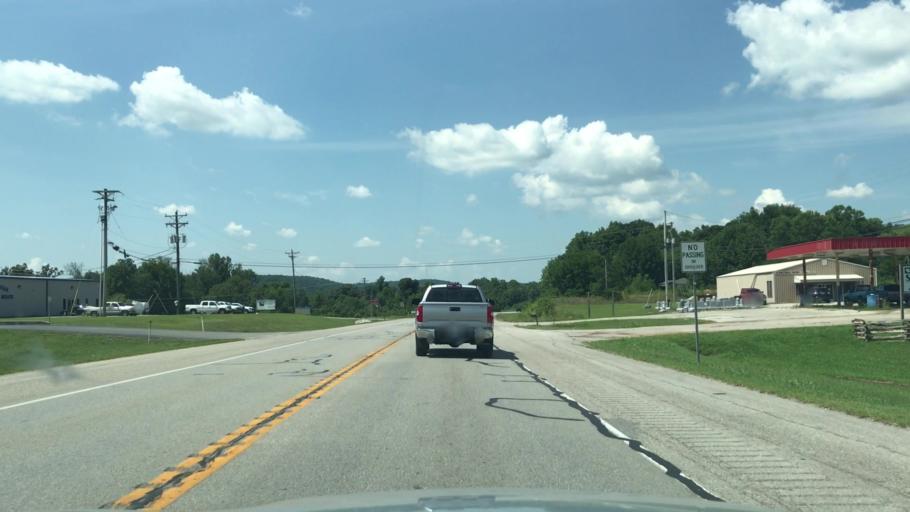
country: US
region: Kentucky
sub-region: Wayne County
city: Monticello
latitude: 36.8085
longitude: -84.9088
